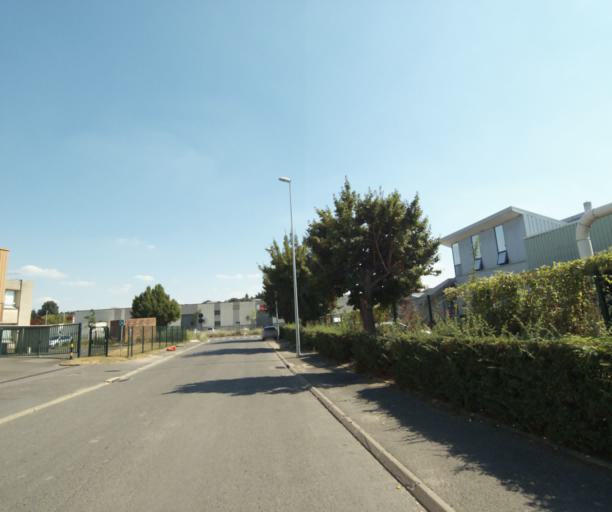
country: FR
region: Ile-de-France
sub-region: Departement de Seine-et-Marne
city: Saint-Thibault-des-Vignes
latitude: 48.8741
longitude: 2.6834
